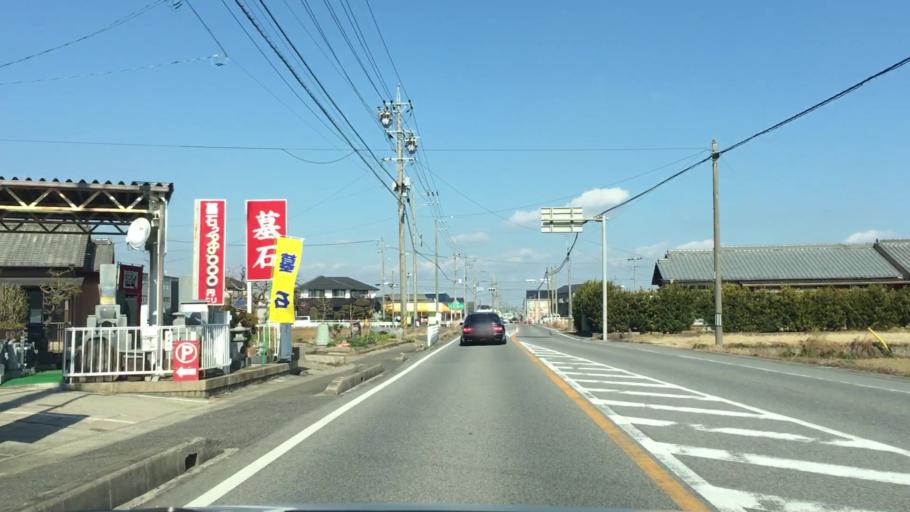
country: JP
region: Aichi
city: Anjo
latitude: 34.9981
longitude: 137.1148
